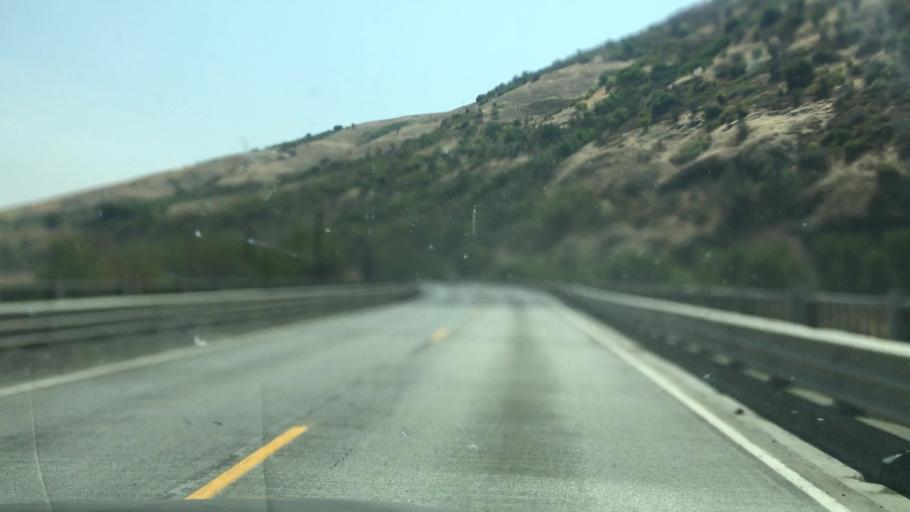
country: US
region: Idaho
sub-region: Nez Perce County
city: Lapwai
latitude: 46.4413
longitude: -116.8450
